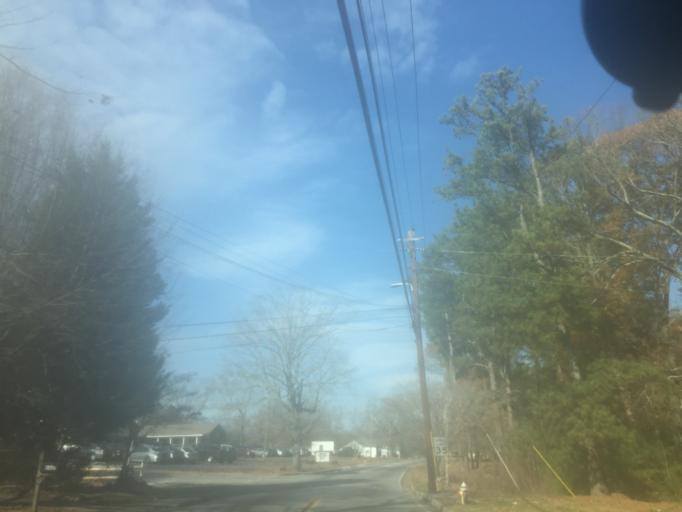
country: US
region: Georgia
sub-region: Clayton County
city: Riverdale
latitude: 33.5683
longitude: -84.4162
